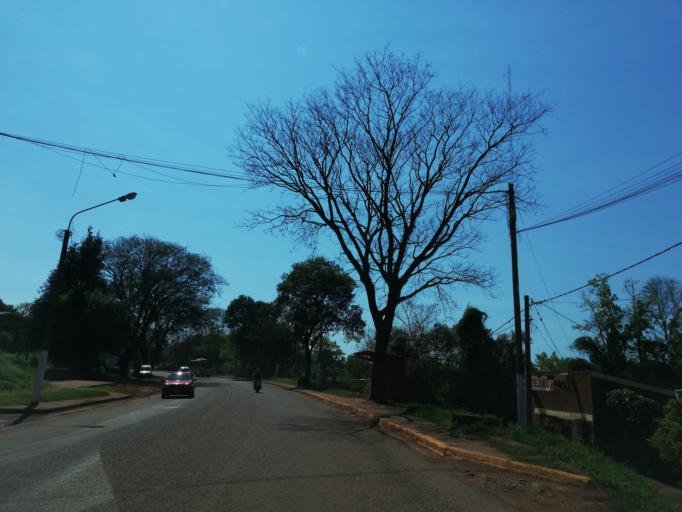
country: AR
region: Misiones
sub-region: Departamento de Eldorado
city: Eldorado
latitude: -26.4089
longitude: -54.6429
